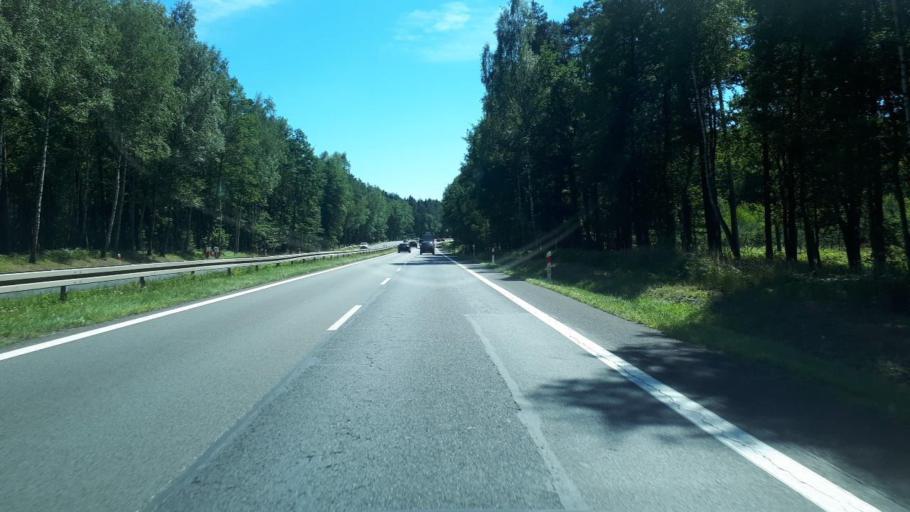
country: PL
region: Silesian Voivodeship
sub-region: Tychy
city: Cielmice
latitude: 50.0816
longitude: 19.0023
